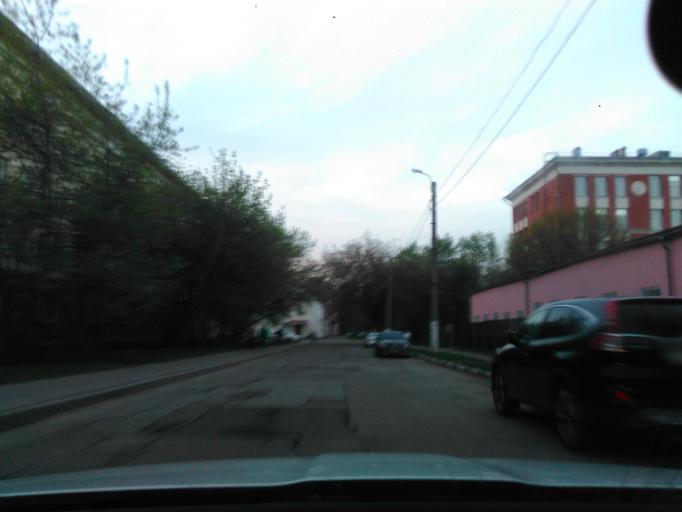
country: RU
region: Moscow
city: Kapotnya
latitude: 55.6388
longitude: 37.7973
